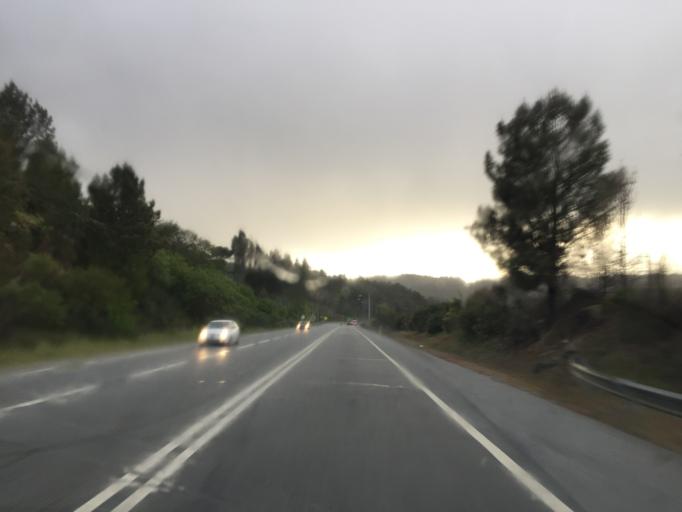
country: PT
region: Viseu
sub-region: Viseu
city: Viseu
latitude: 40.6054
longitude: -7.9719
